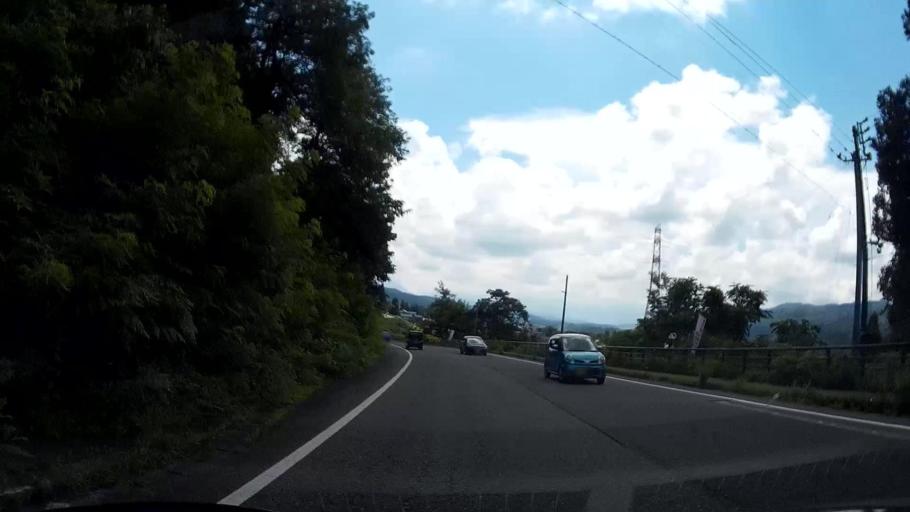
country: JP
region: Niigata
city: Tokamachi
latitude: 37.0904
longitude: 138.7244
